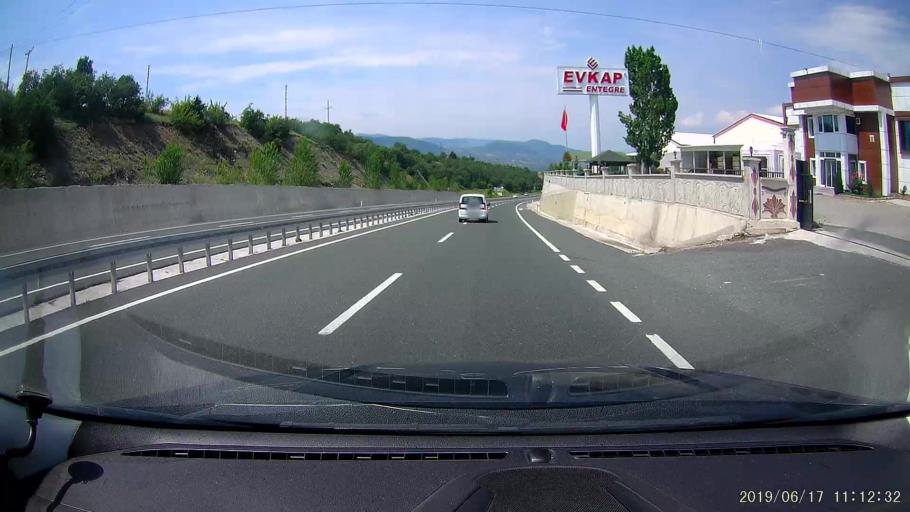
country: TR
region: Kastamonu
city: Tosya
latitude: 40.9709
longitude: 33.9934
